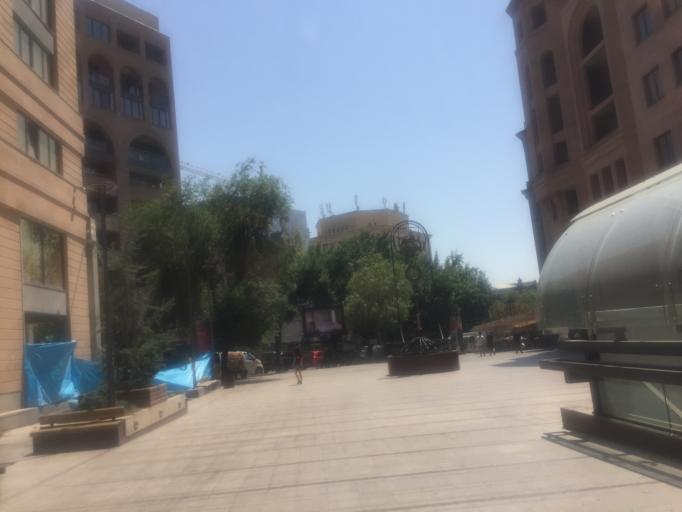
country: AM
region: Yerevan
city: Yerevan
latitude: 40.1805
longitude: 44.5146
